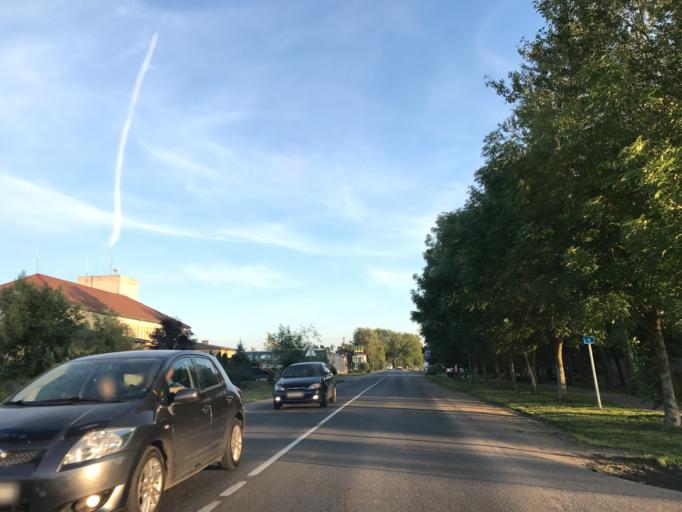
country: RU
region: Kaliningrad
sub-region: Zelenogradskiy Rayon
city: Zelenogradsk
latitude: 54.9522
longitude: 20.4704
